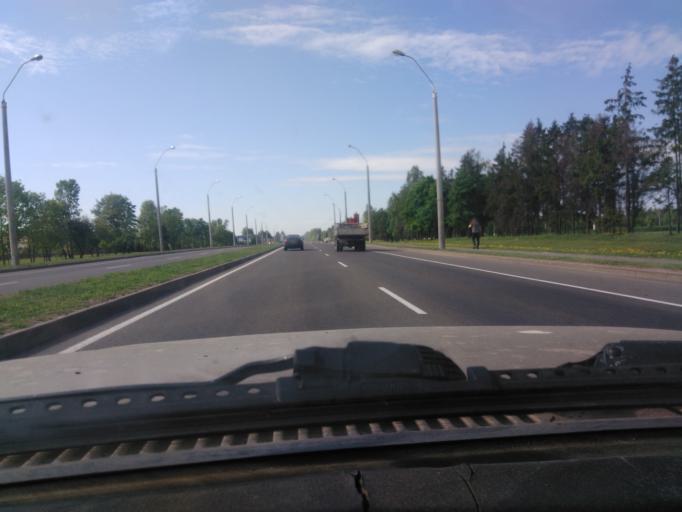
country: BY
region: Mogilev
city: Buynichy
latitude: 53.8654
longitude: 30.2598
